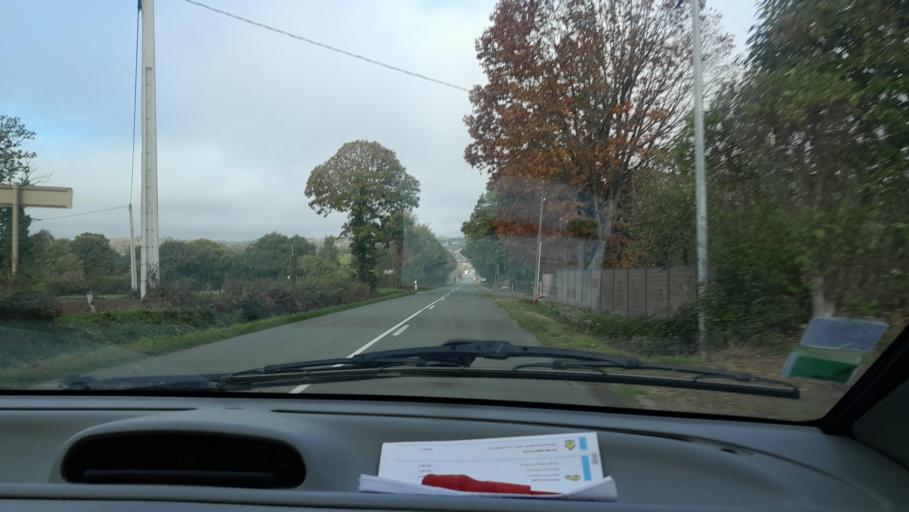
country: FR
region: Brittany
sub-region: Departement d'Ille-et-Vilaine
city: Luitre
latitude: 48.2610
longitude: -1.1330
